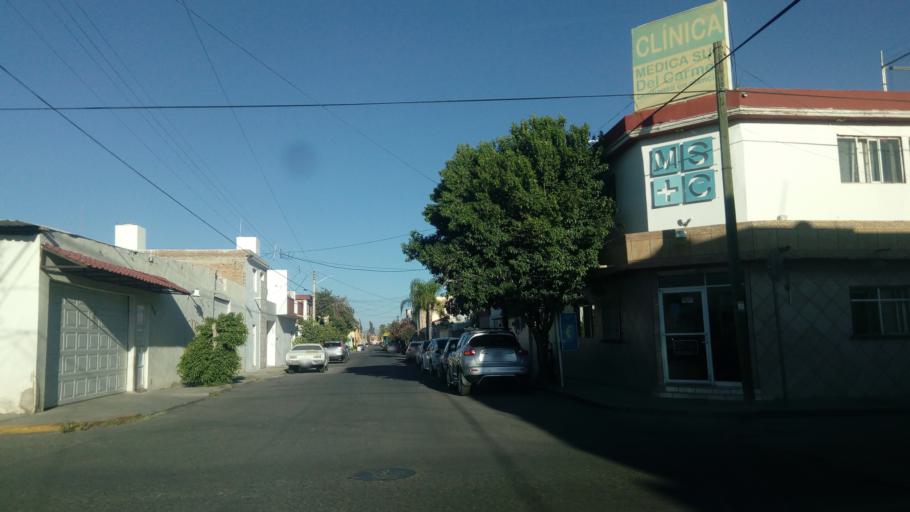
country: MX
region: Durango
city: Victoria de Durango
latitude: 24.0119
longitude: -104.6827
